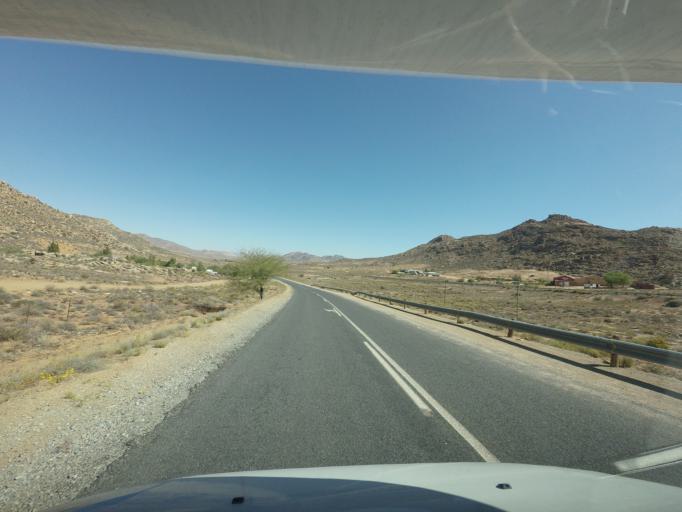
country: ZA
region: Northern Cape
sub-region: Namakwa District Municipality
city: Springbok
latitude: -29.6716
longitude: 17.8980
